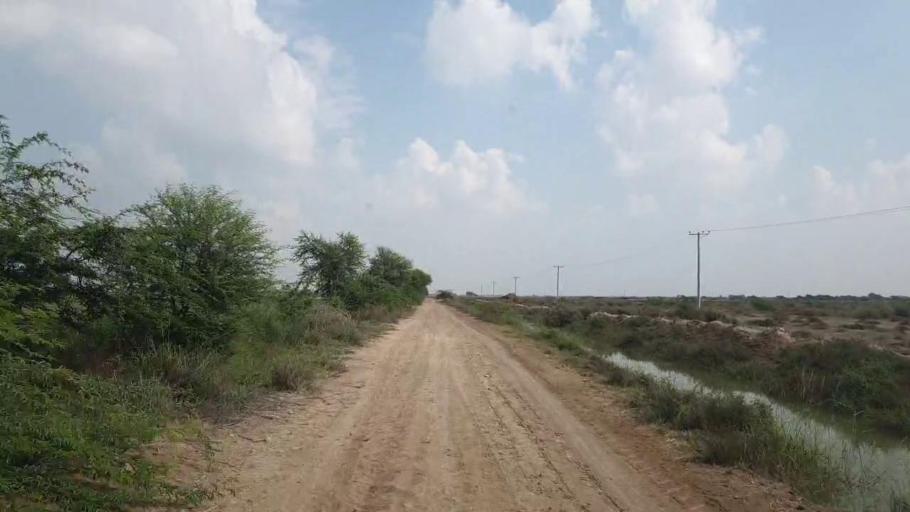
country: PK
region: Sindh
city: Badin
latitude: 24.5328
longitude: 68.6244
